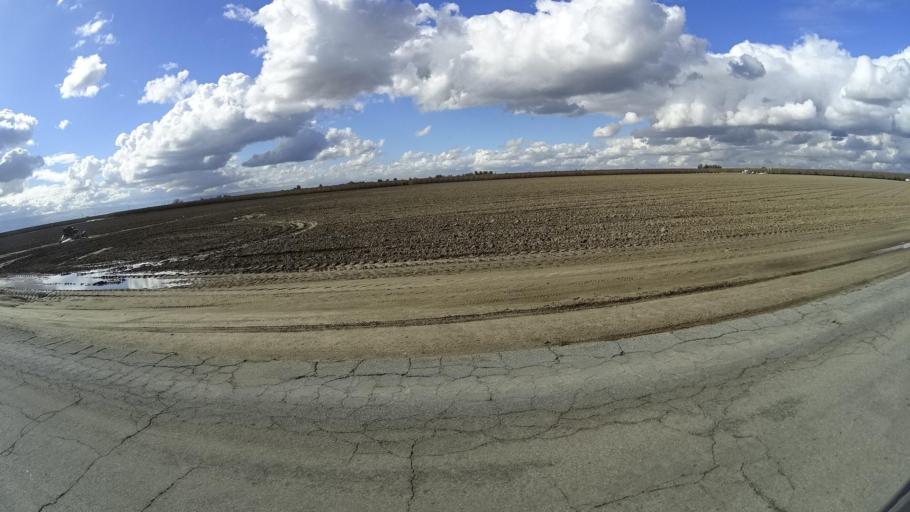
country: US
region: California
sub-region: Kern County
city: Greenfield
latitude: 35.2421
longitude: -119.0569
